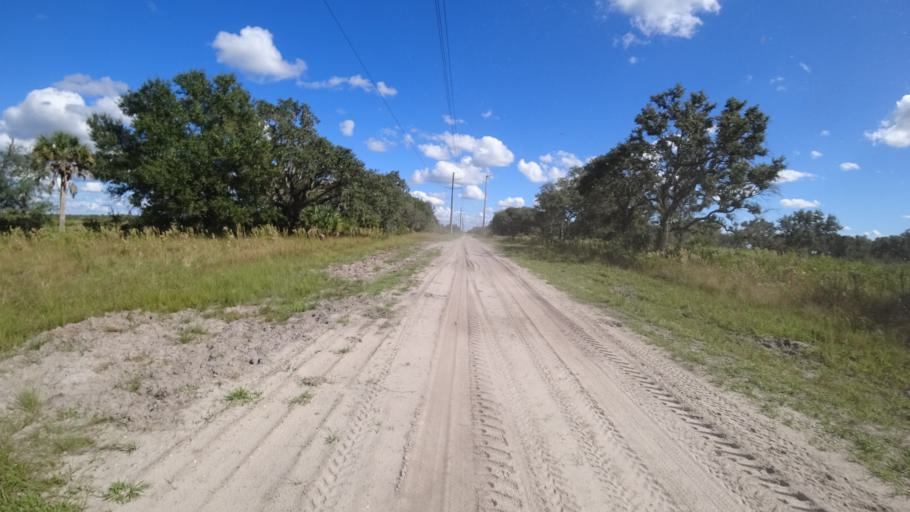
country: US
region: Florida
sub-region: Sarasota County
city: Lake Sarasota
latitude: 27.2426
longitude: -82.2635
